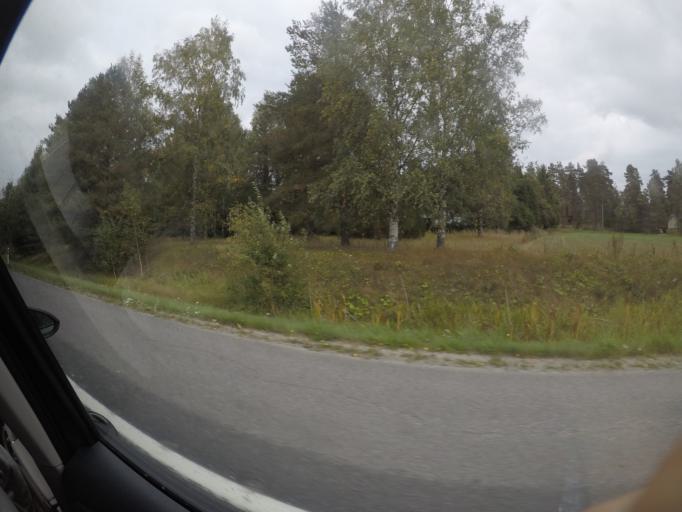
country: FI
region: Haeme
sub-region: Haemeenlinna
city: Parola
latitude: 61.0465
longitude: 24.3973
